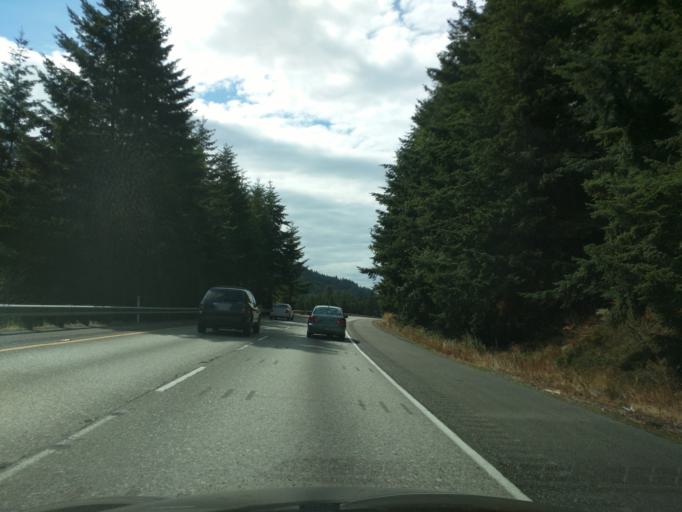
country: US
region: Washington
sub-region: Whatcom County
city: Geneva
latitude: 48.6930
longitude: -122.4473
